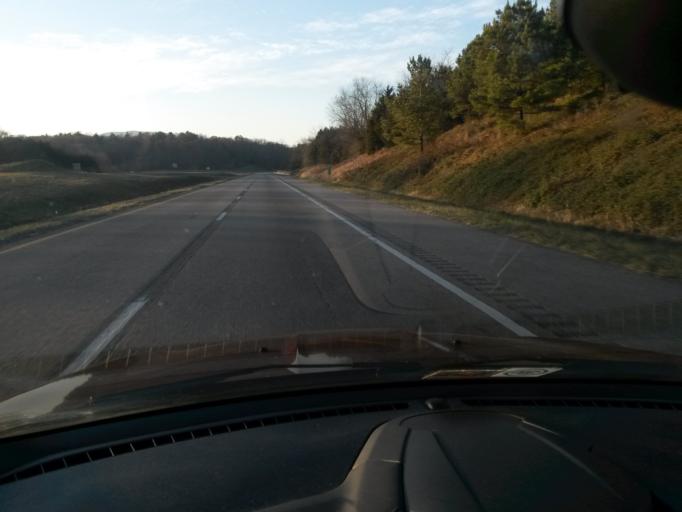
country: US
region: Virginia
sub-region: Rockbridge County
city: East Lexington
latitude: 37.8073
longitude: -79.4290
